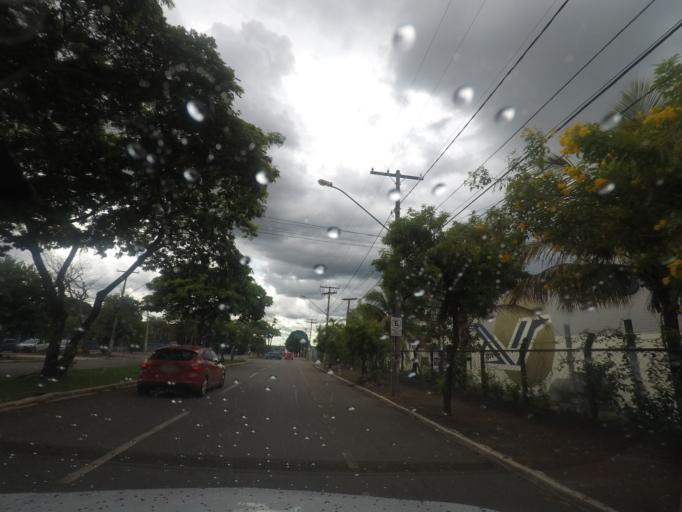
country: BR
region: Goias
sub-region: Goiania
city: Goiania
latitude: -16.6320
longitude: -49.2300
